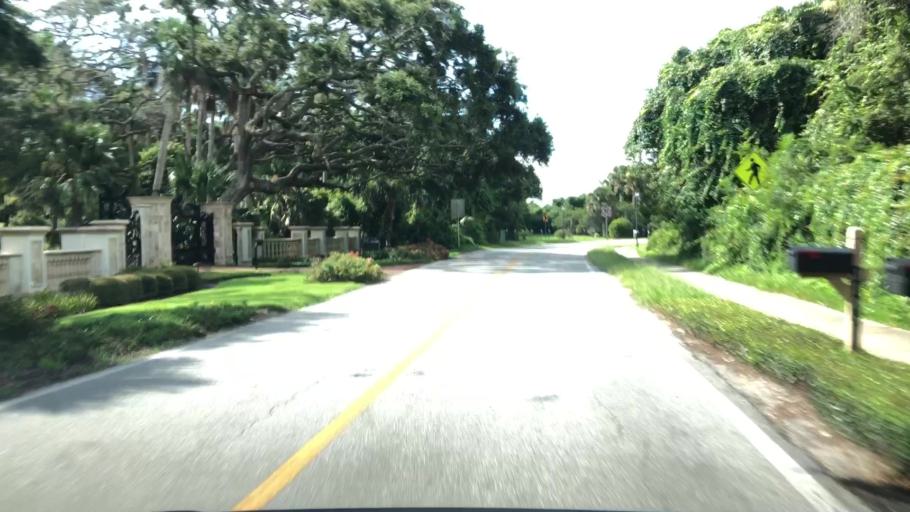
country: US
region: Florida
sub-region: Saint Johns County
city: Sawgrass
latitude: 30.1635
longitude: -81.3576
